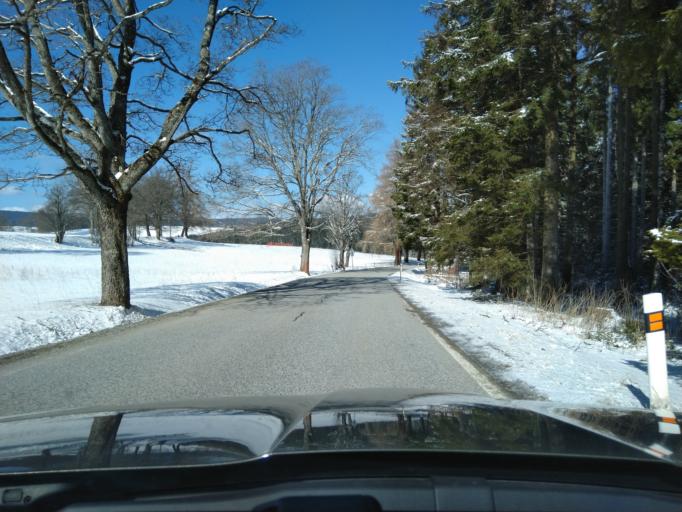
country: CZ
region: Jihocesky
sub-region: Okres Prachatice
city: Zdikov
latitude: 49.0452
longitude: 13.6732
